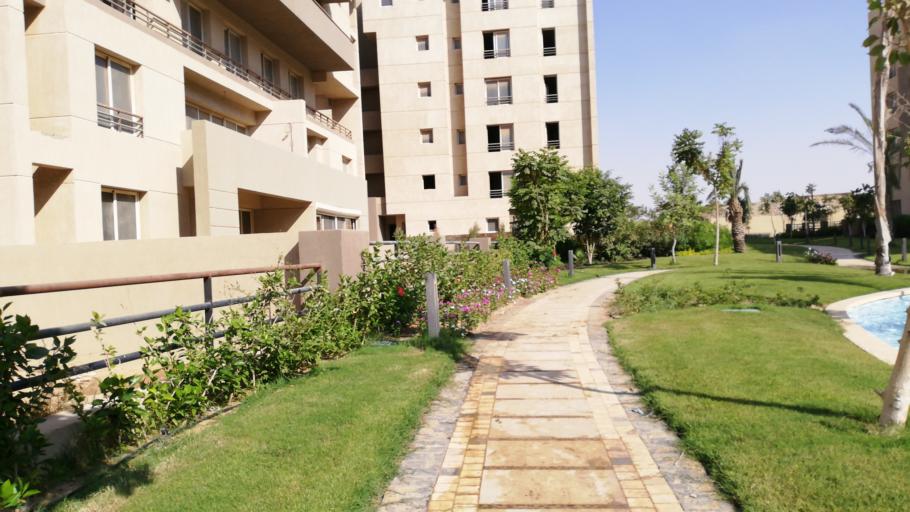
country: EG
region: Muhafazat al Qalyubiyah
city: Al Khankah
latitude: 29.9999
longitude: 31.5553
